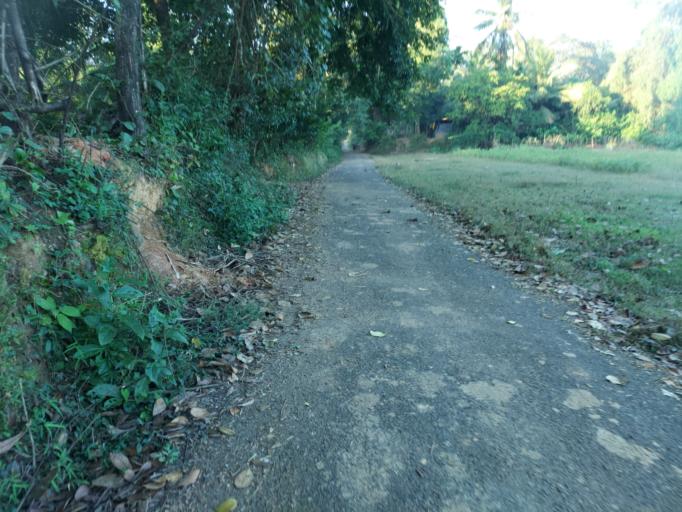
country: IN
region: Maharashtra
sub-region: Sindhudurg
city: Kudal
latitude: 16.0391
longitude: 73.6798
